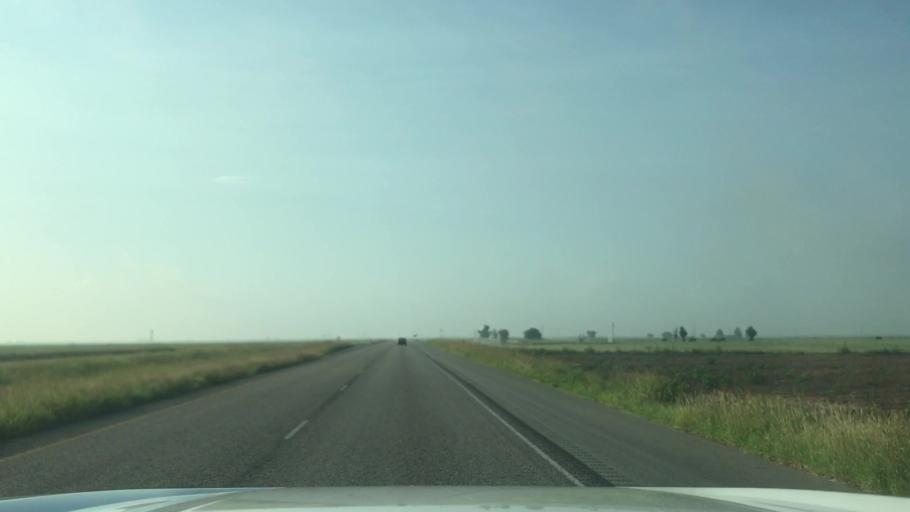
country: US
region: Texas
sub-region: Lubbock County
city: Slaton
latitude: 33.3389
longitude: -101.5403
